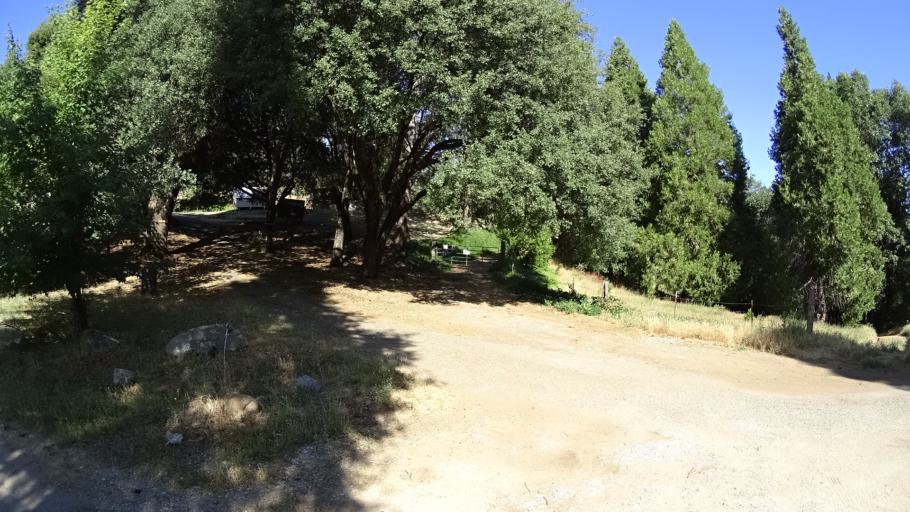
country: US
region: California
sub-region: Amador County
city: Pioneer
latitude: 38.3944
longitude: -120.5824
